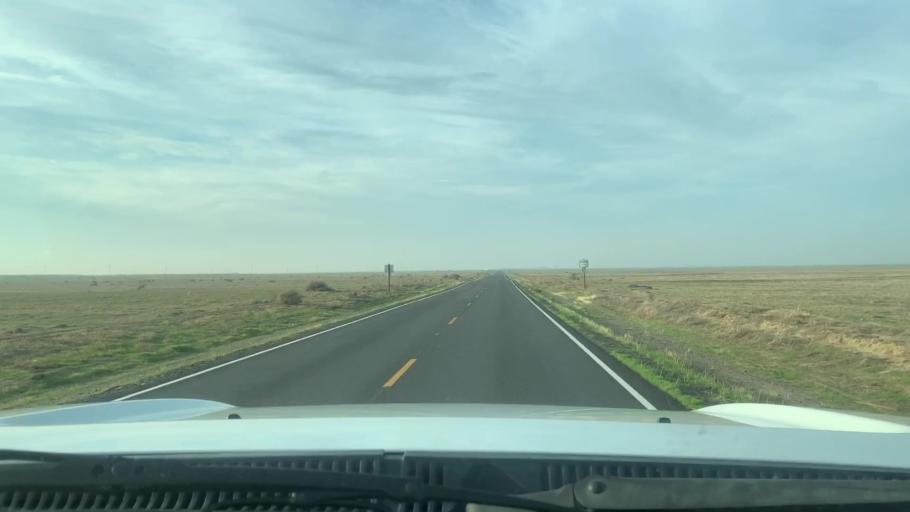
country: US
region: California
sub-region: Kern County
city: Lost Hills
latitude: 35.5730
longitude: -119.8161
